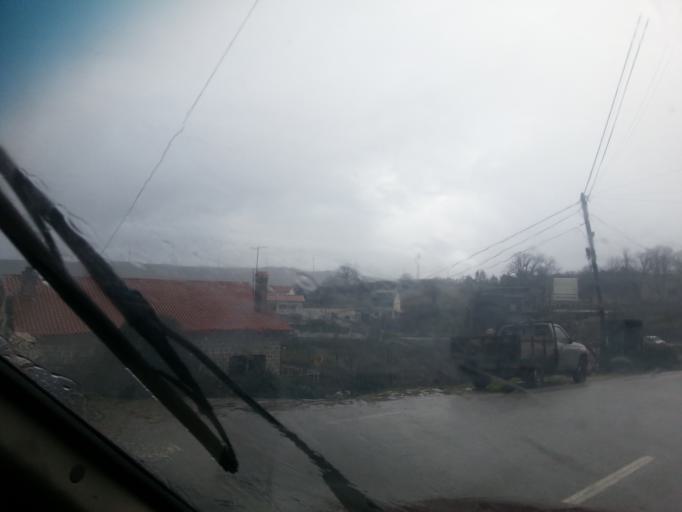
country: PT
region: Guarda
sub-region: Guarda
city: Guarda
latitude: 40.5437
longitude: -7.3176
